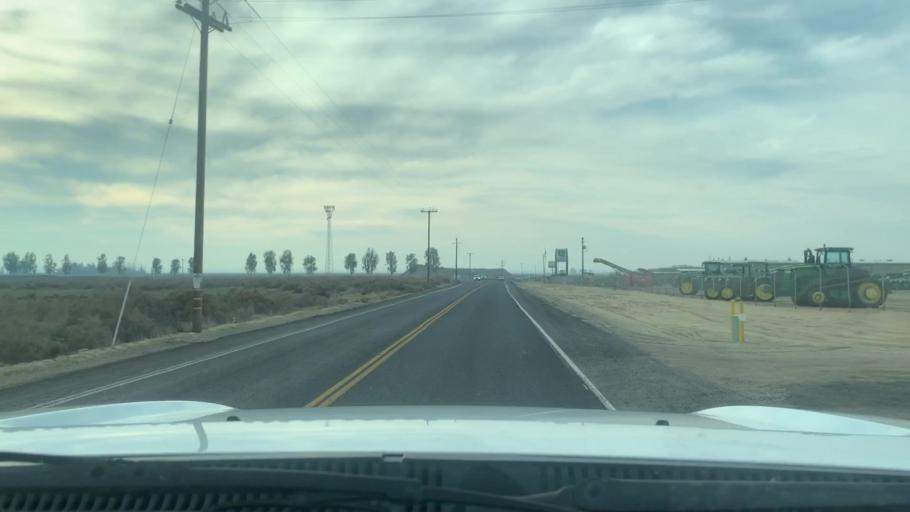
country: US
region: California
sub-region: Kern County
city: Buttonwillow
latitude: 35.4996
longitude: -119.5432
